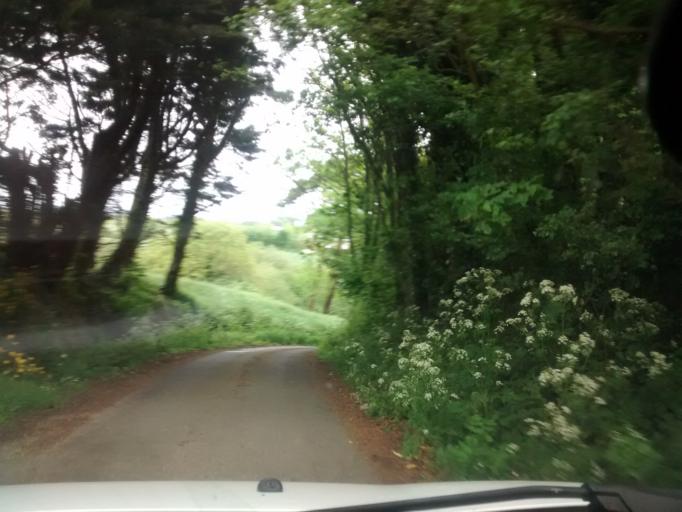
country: FR
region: Brittany
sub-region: Departement des Cotes-d'Armor
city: Plougrescant
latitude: 48.8419
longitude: -3.2204
